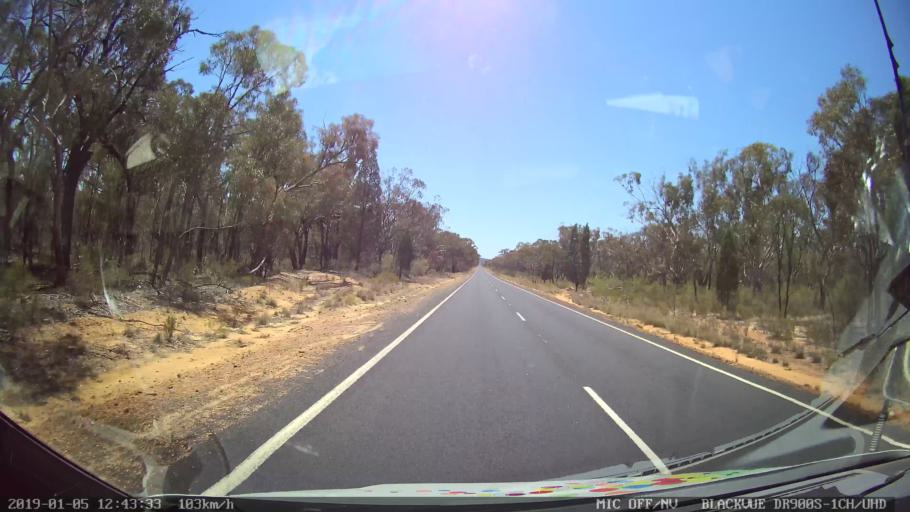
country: AU
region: New South Wales
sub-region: Warrumbungle Shire
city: Coonabarabran
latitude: -31.1469
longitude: 149.5255
